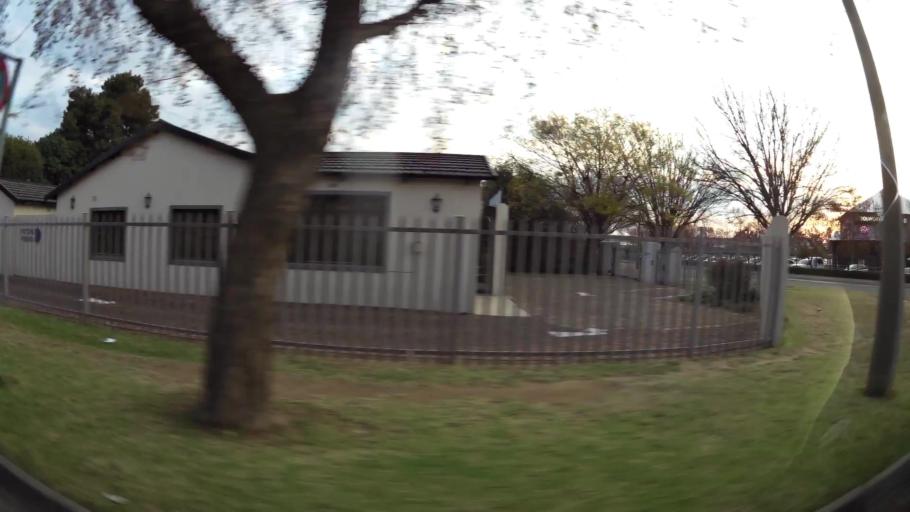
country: ZA
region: Gauteng
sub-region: Ekurhuleni Metropolitan Municipality
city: Benoni
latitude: -26.1630
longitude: 28.3054
